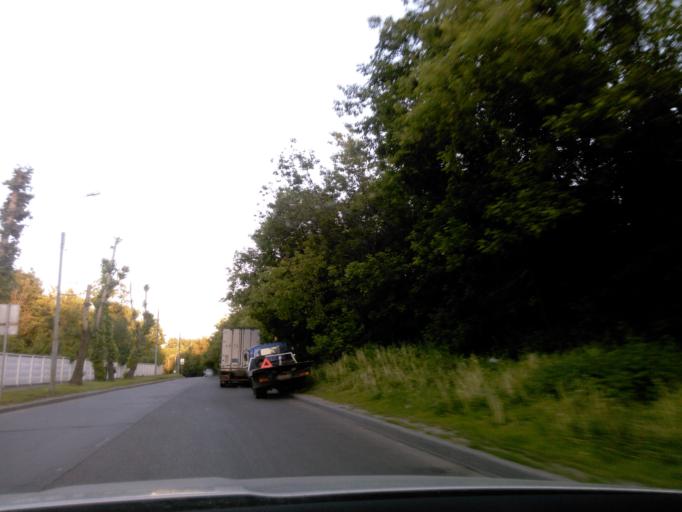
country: RU
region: Moscow
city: Taganskiy
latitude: 55.7312
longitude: 37.6891
